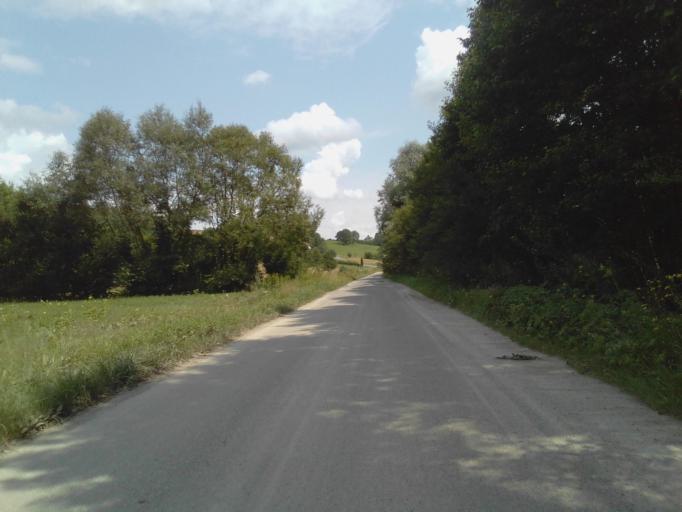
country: PL
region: Subcarpathian Voivodeship
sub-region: Powiat strzyzowski
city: Frysztak
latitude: 49.8177
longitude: 21.5893
